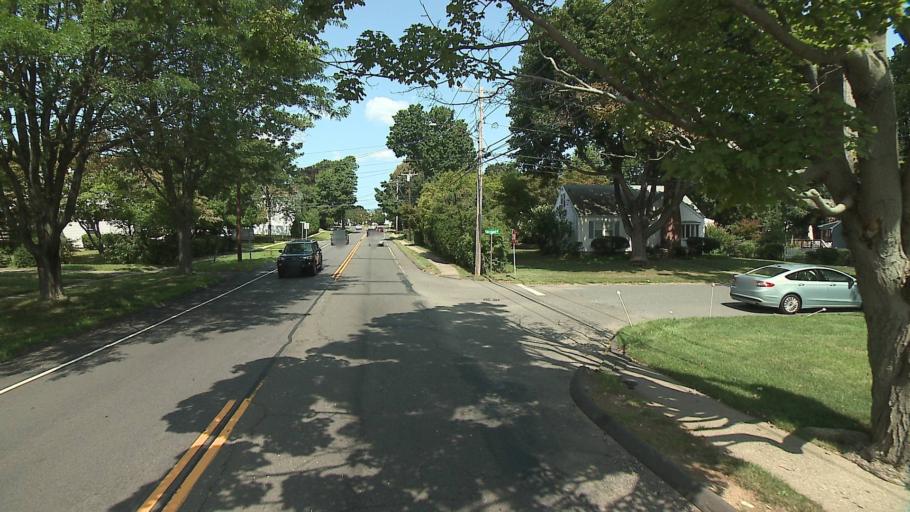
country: US
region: Connecticut
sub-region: Fairfield County
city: Stratford
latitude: 41.2173
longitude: -73.1194
